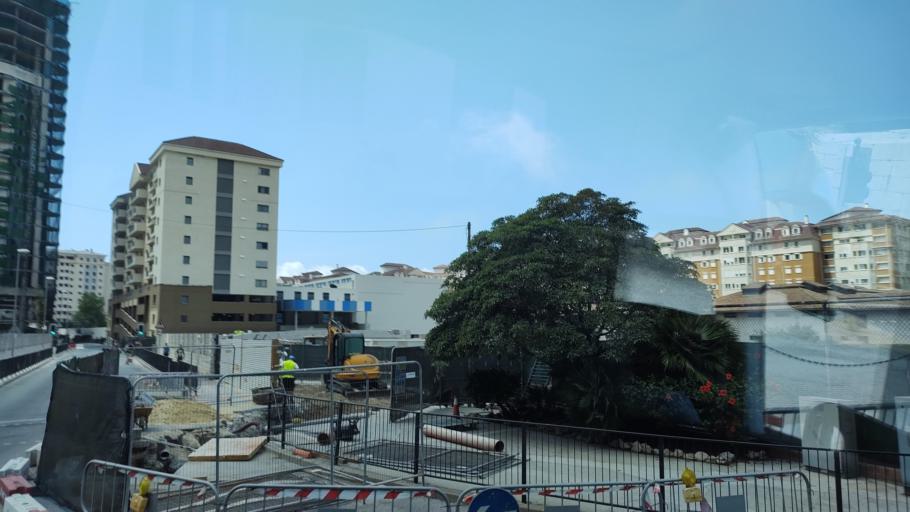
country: GI
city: Gibraltar
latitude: 36.1432
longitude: -5.3553
